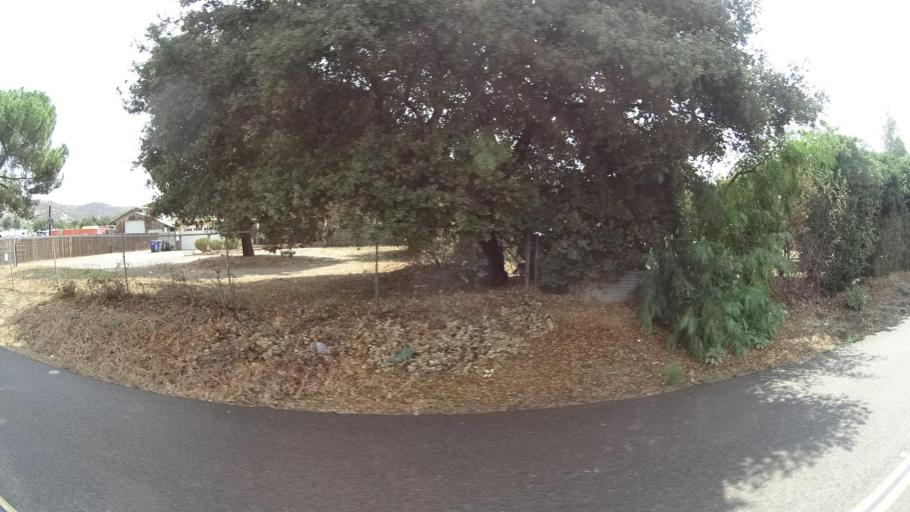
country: US
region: California
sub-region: San Diego County
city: Ramona
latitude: 33.0724
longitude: -116.8451
